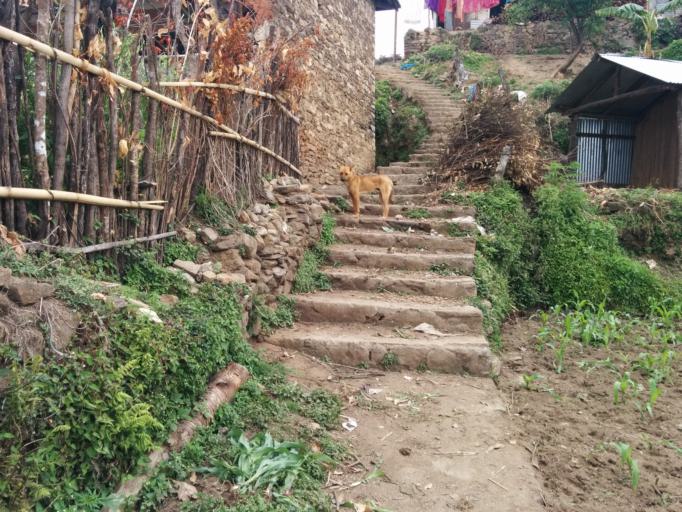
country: NP
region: Central Region
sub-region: Bagmati Zone
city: Bhaktapur
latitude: 27.7800
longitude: 85.4320
